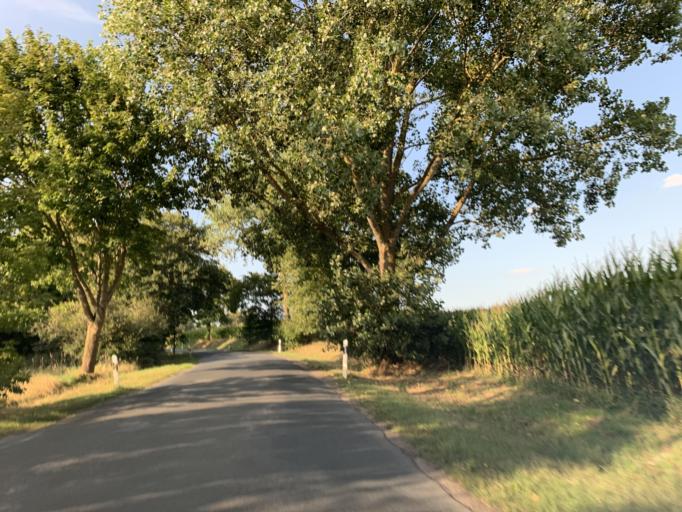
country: DE
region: Mecklenburg-Vorpommern
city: Loitz
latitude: 53.3669
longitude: 13.3590
